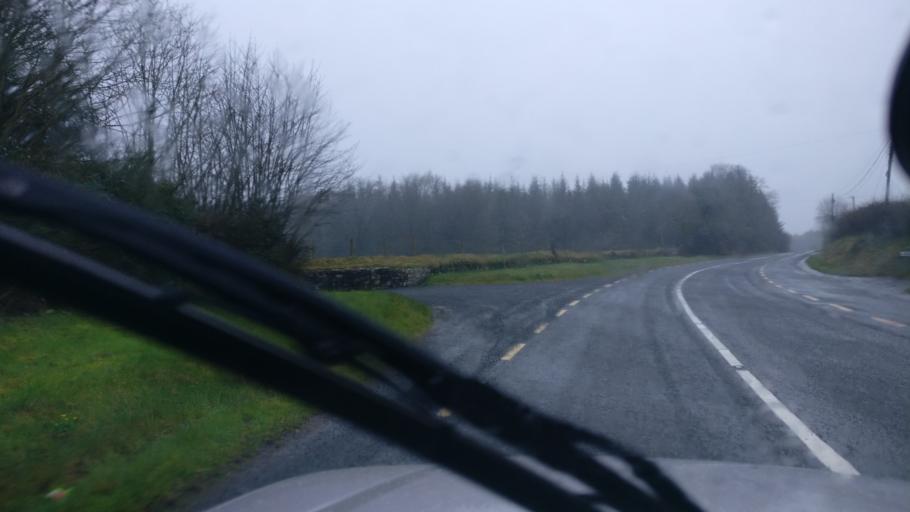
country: IE
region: Connaught
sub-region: County Galway
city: Loughrea
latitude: 53.1395
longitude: -8.4682
